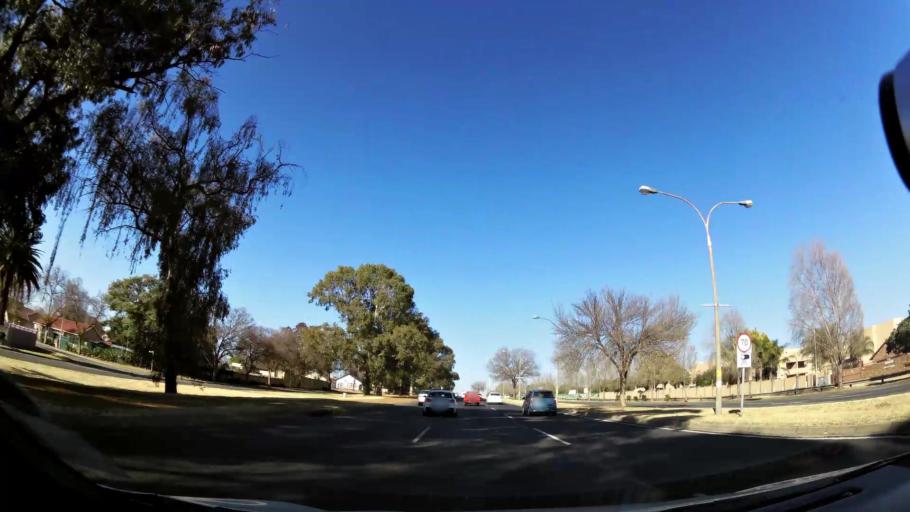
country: ZA
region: Gauteng
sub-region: Ekurhuleni Metropolitan Municipality
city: Germiston
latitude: -26.2950
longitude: 28.1185
